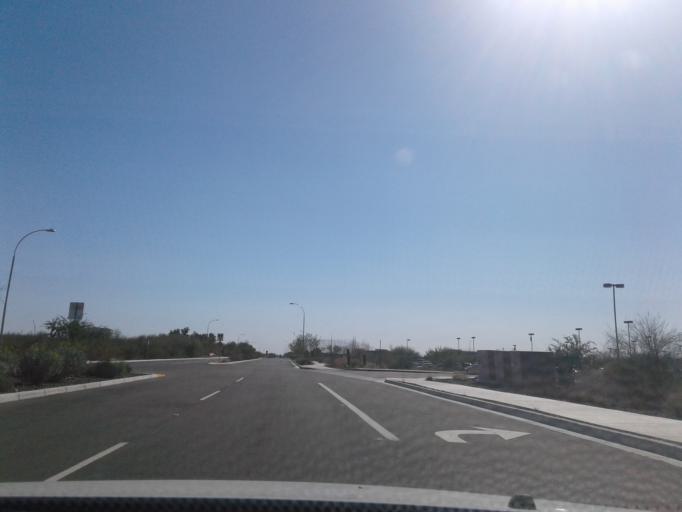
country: US
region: Arizona
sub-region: Maricopa County
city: Scottsdale
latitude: 33.5554
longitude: -111.8741
